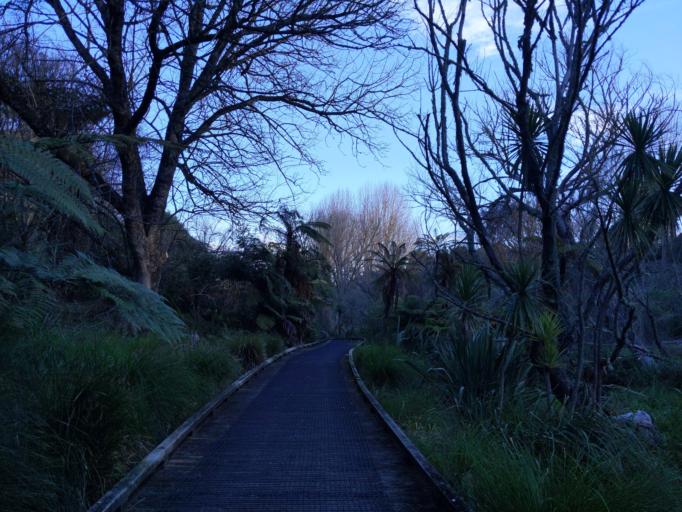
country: NZ
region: Waikato
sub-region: Hamilton City
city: Hamilton
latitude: -37.7388
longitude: 175.2761
